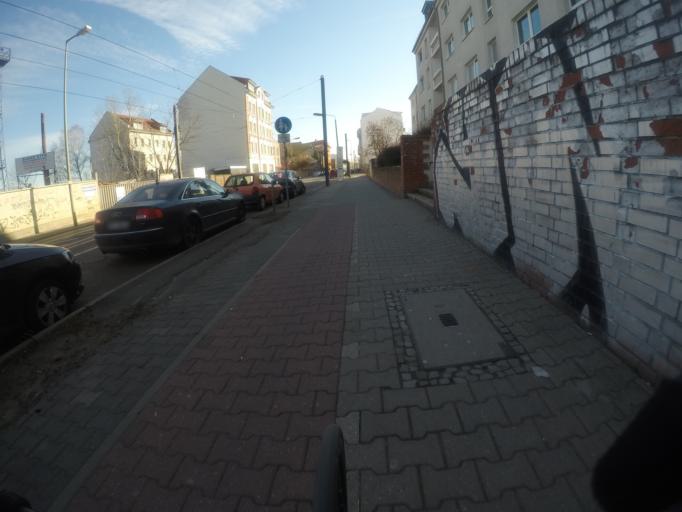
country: DE
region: Berlin
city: Kopenick Bezirk
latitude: 52.4412
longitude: 13.5700
